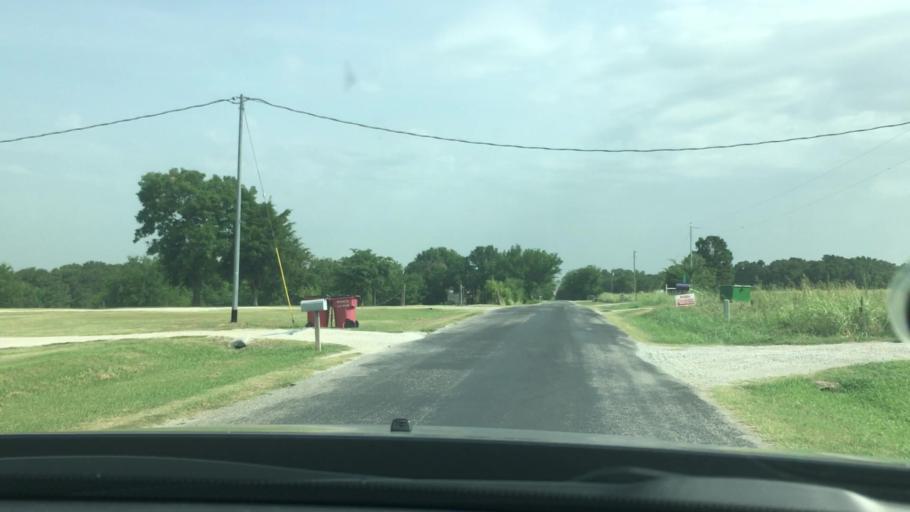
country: US
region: Oklahoma
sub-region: Garvin County
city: Pauls Valley
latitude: 34.8059
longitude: -97.1955
